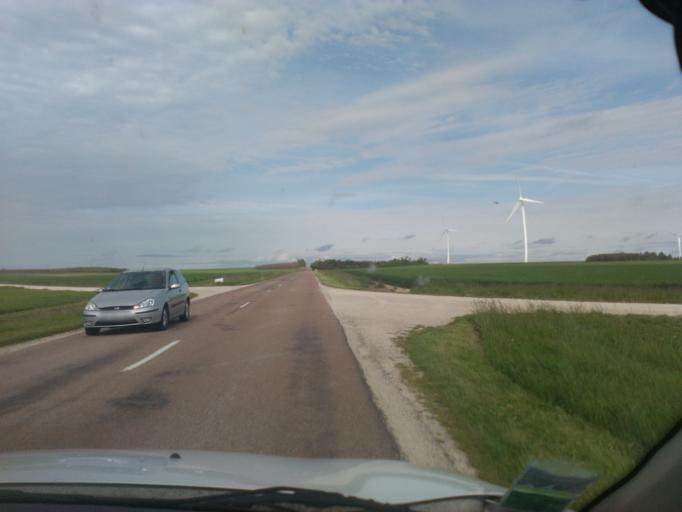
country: FR
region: Champagne-Ardenne
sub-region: Departement de l'Aube
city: Payns
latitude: 48.3657
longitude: 3.9411
